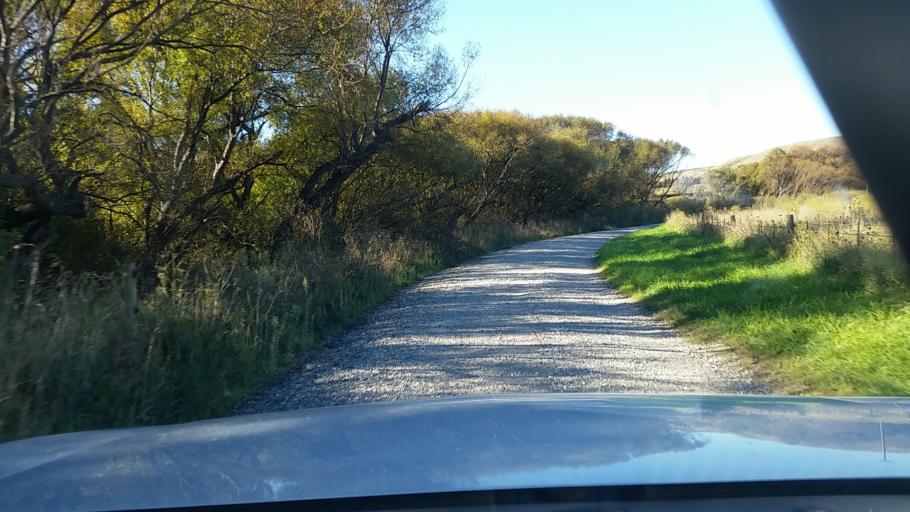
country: NZ
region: Marlborough
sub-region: Marlborough District
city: Blenheim
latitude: -41.6783
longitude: 174.1364
